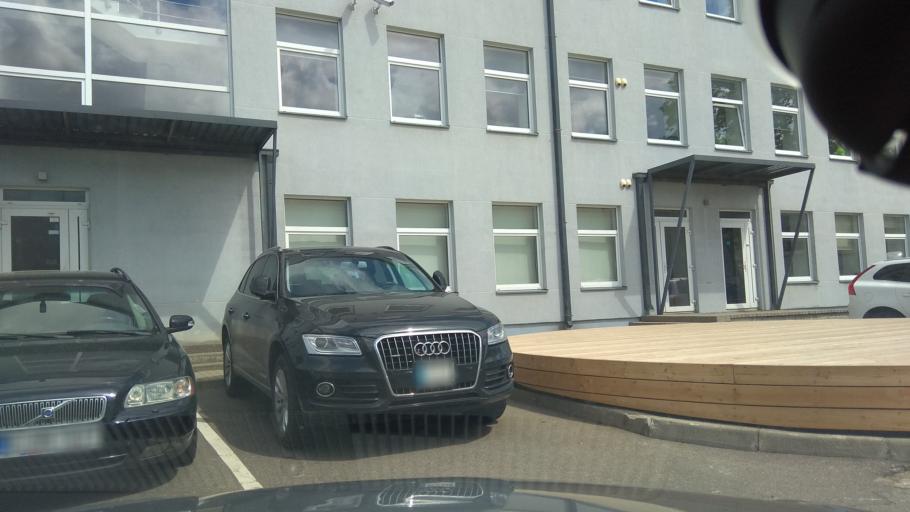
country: LT
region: Vilnius County
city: Vilkpede
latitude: 54.6644
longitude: 25.2473
